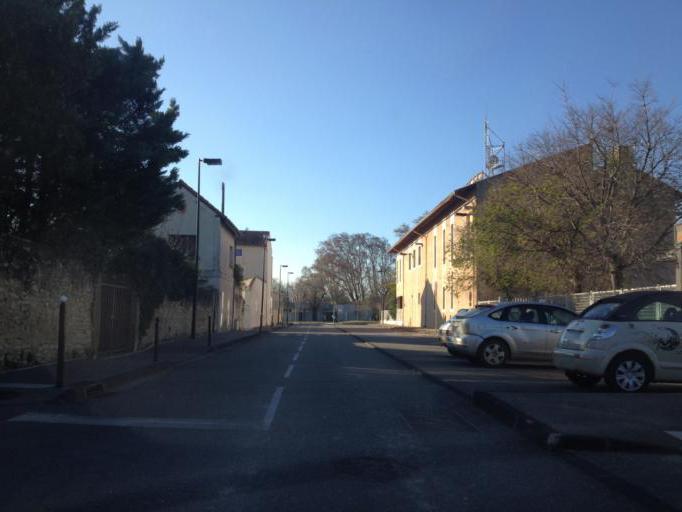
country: FR
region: Provence-Alpes-Cote d'Azur
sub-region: Departement du Vaucluse
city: Orange
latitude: 44.1330
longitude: 4.7996
